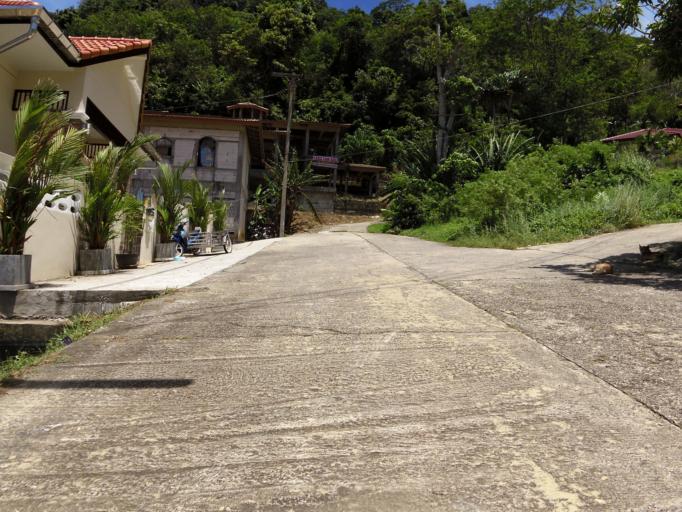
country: TH
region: Phuket
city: Ban Karon
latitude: 7.8508
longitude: 98.3056
